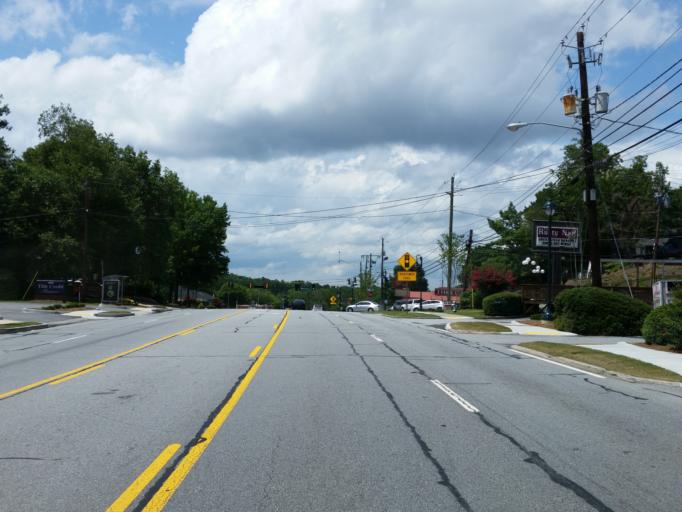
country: US
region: Georgia
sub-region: Fulton County
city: Roswell
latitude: 33.9873
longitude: -84.3509
